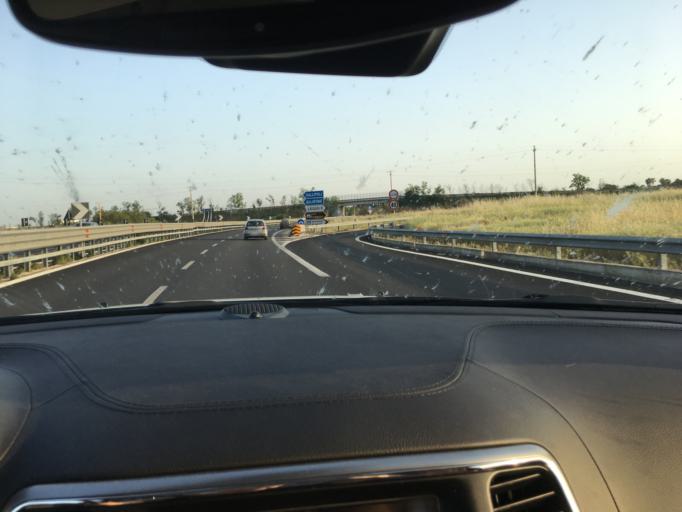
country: IT
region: Apulia
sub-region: Provincia di Lecce
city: Lequile
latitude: 40.2917
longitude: 18.1330
